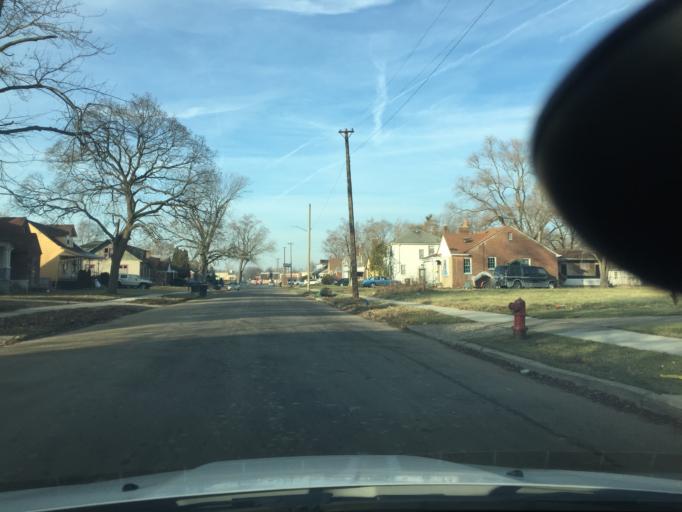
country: US
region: Michigan
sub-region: Macomb County
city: Eastpointe
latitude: 42.4382
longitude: -82.9717
